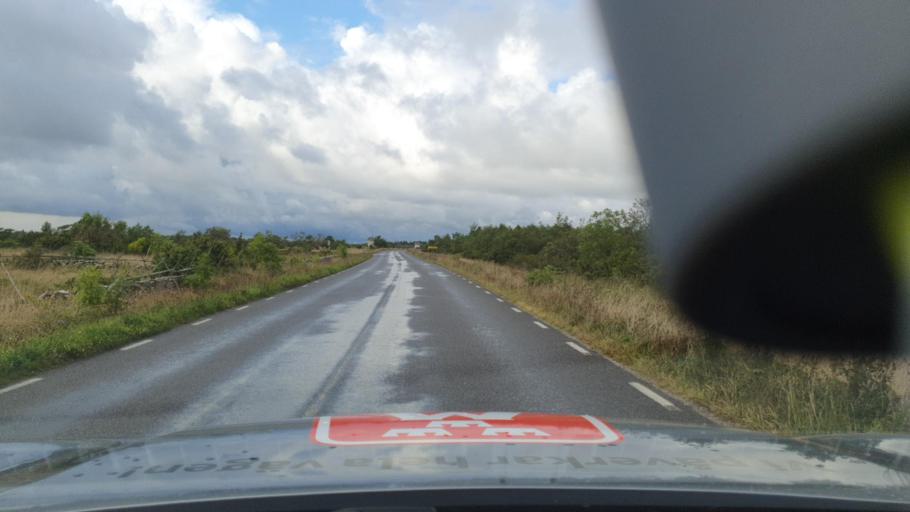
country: SE
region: Gotland
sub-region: Gotland
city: Hemse
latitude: 56.9969
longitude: 18.2489
